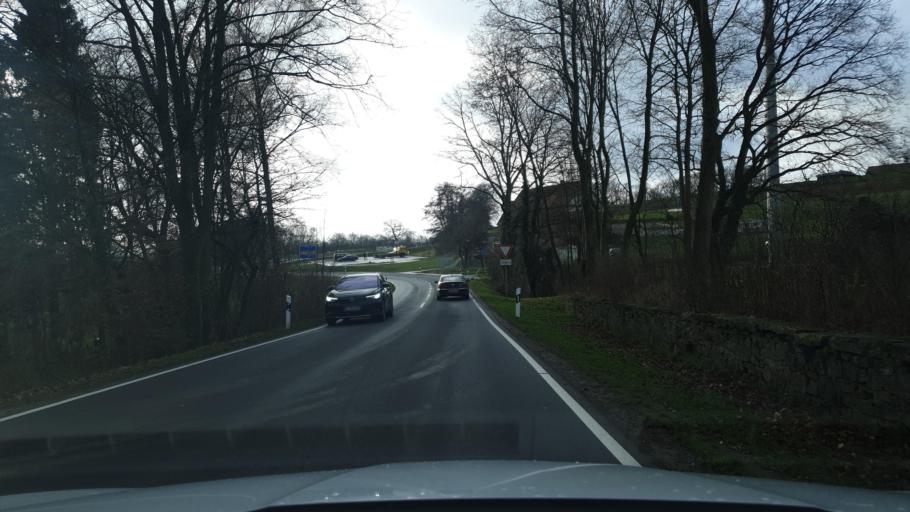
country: DE
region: North Rhine-Westphalia
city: Bad Oeynhausen
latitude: 52.1469
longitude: 8.7824
